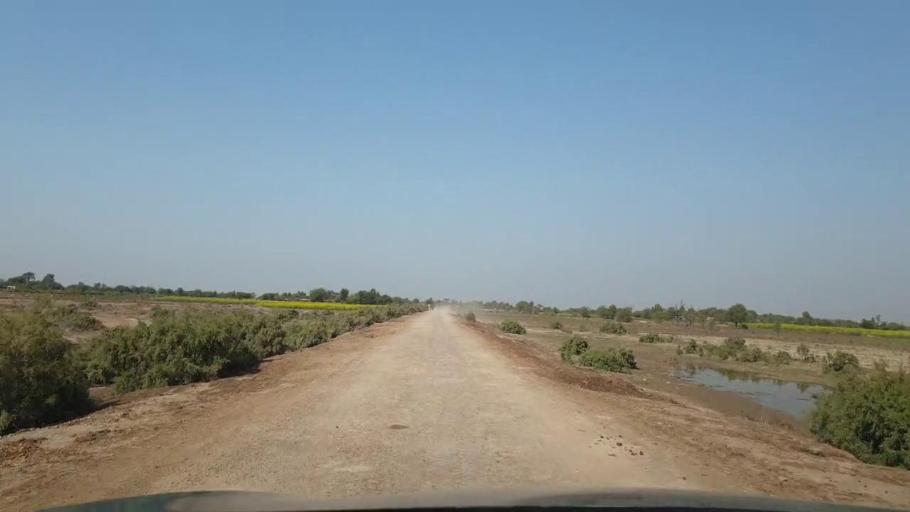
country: PK
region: Sindh
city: Berani
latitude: 25.6221
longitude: 68.8454
